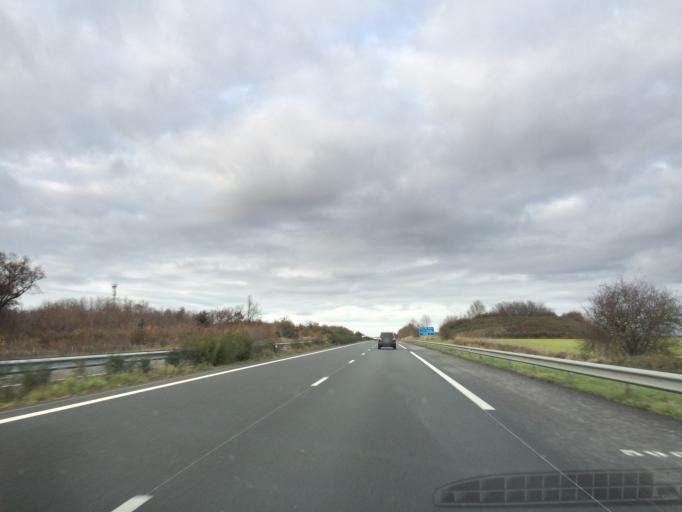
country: FR
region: Poitou-Charentes
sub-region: Departement des Deux-Sevres
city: Beauvoir-sur-Niort
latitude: 46.0888
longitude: -0.5321
